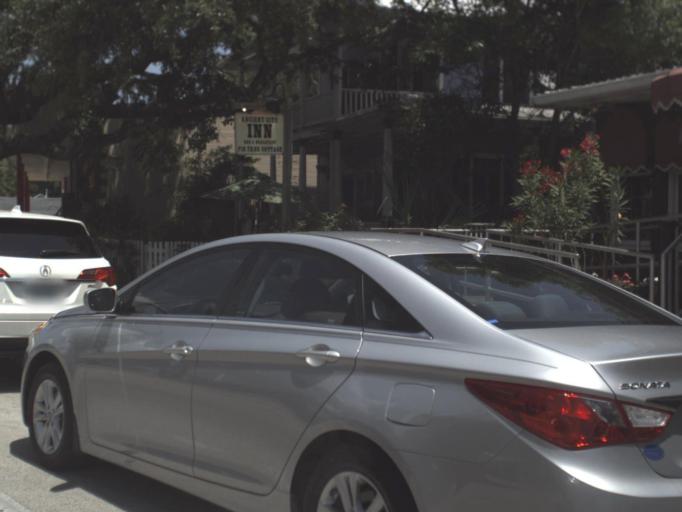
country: US
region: Florida
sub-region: Saint Johns County
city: Saint Augustine
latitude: 29.9009
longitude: -81.3154
